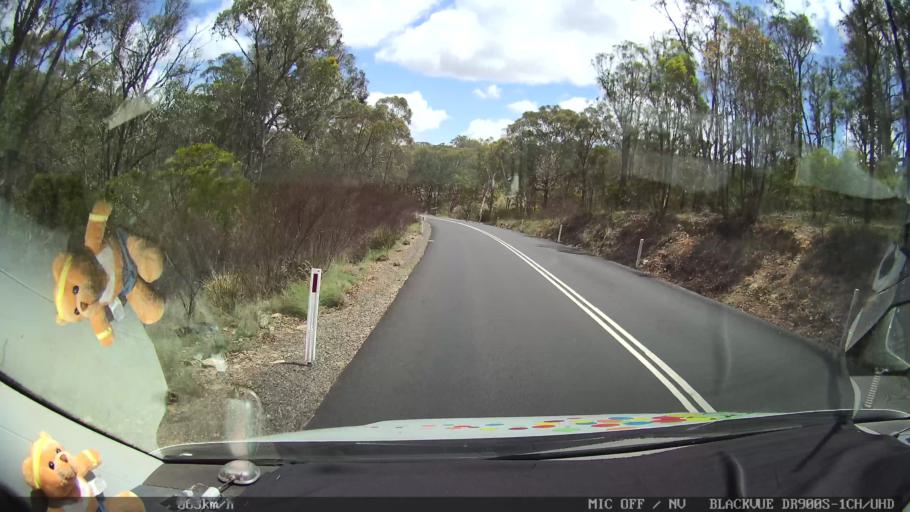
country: AU
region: New South Wales
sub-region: Glen Innes Severn
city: Glen Innes
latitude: -29.5649
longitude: 151.6691
